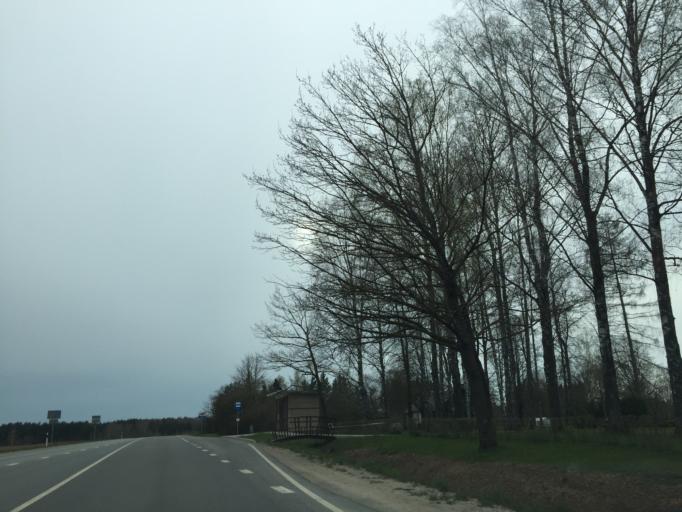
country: LV
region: Ludzas Rajons
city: Ludza
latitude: 56.5362
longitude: 27.6801
